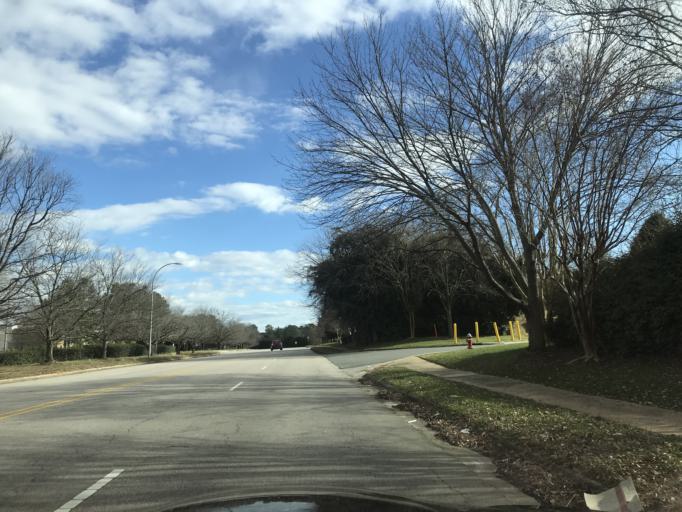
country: US
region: North Carolina
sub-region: Wake County
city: Cary
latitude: 35.7583
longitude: -78.7375
